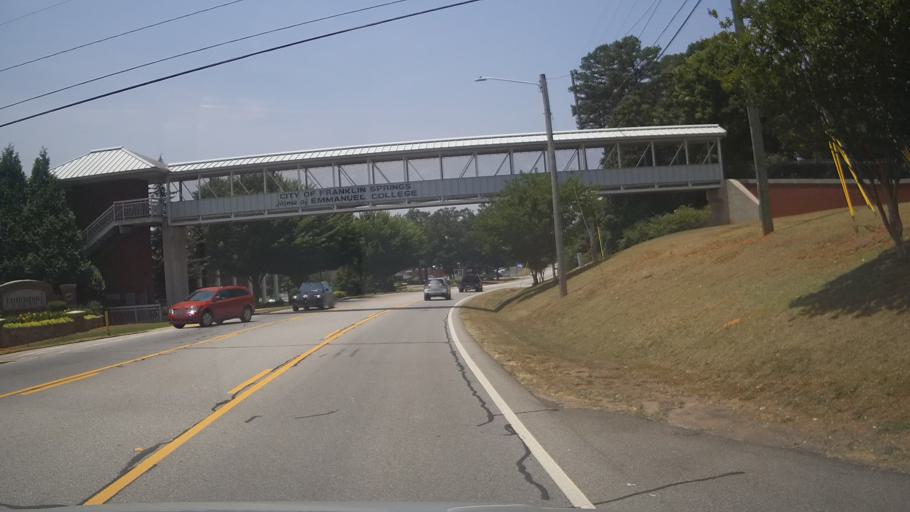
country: US
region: Georgia
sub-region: Hart County
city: Royston
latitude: 34.2841
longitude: -83.1473
